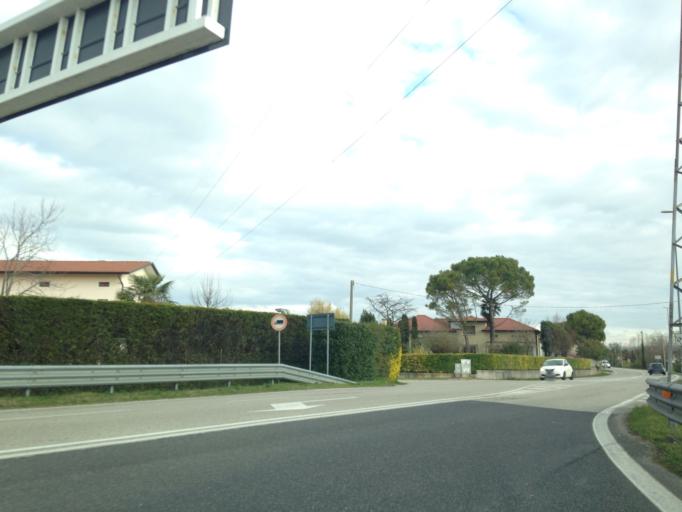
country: IT
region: Friuli Venezia Giulia
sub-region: Provincia di Pordenone
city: Porcia
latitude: 45.9456
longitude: 12.6210
